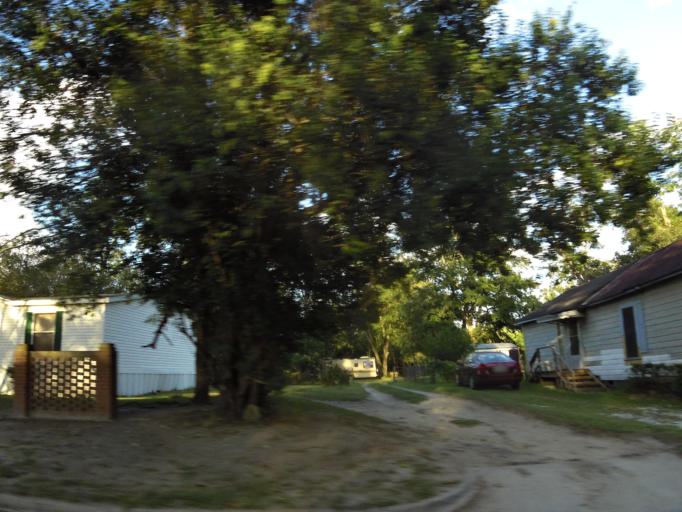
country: US
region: Georgia
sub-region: Lowndes County
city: Valdosta
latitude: 30.8246
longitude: -83.2725
